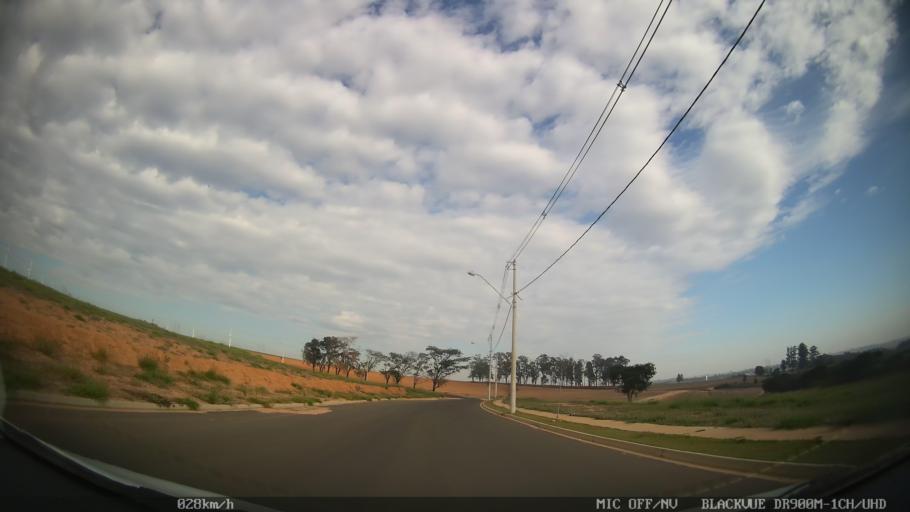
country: BR
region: Sao Paulo
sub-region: Americana
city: Americana
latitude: -22.7109
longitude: -47.3785
